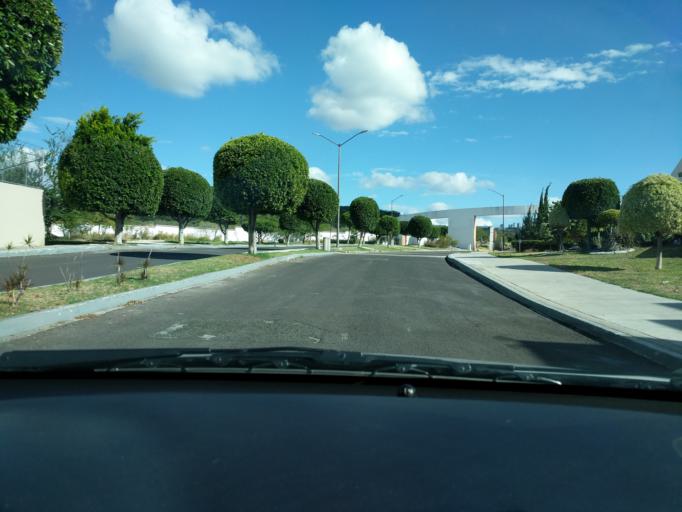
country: MX
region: Queretaro
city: La Canada
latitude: 20.5839
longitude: -100.3354
